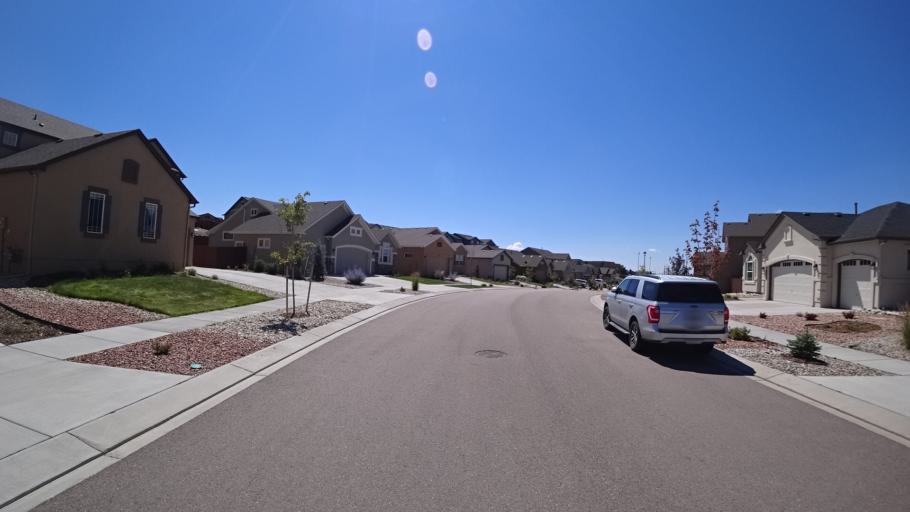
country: US
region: Colorado
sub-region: El Paso County
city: Black Forest
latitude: 38.9904
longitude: -104.7648
